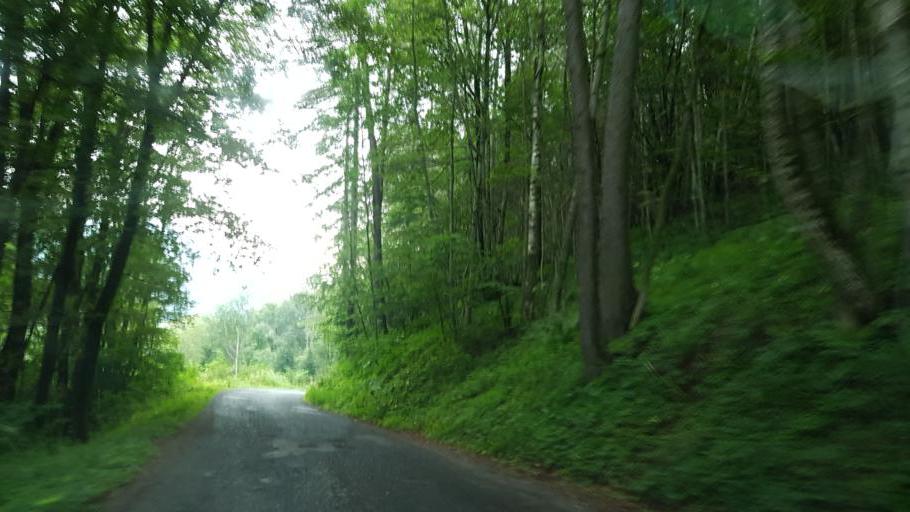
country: IT
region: Piedmont
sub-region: Provincia di Cuneo
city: Sampeyre
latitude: 44.5765
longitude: 7.1734
